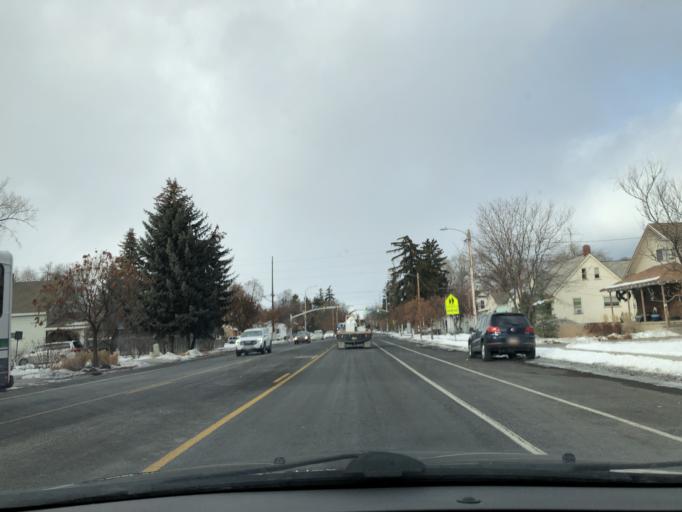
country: US
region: Utah
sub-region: Cache County
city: Logan
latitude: 41.7246
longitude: -111.8326
